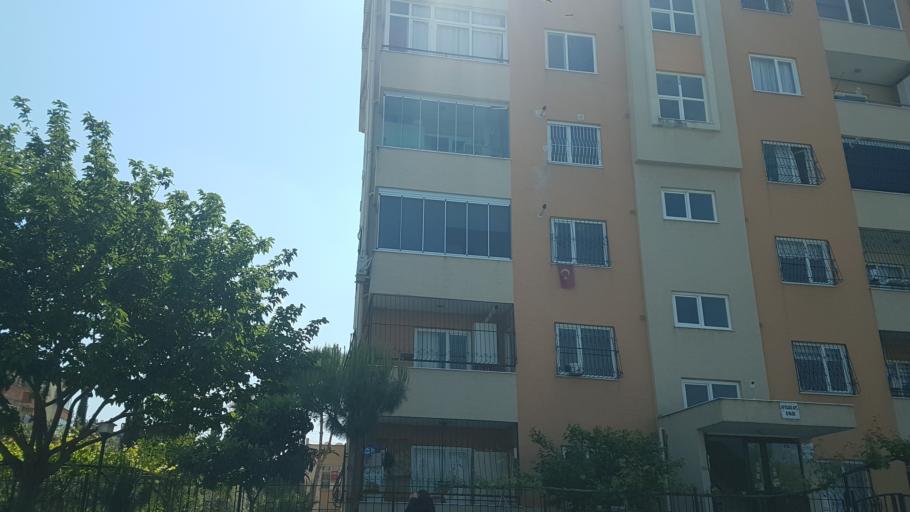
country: TR
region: Adana
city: Yuregir
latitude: 37.0182
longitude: 35.3743
